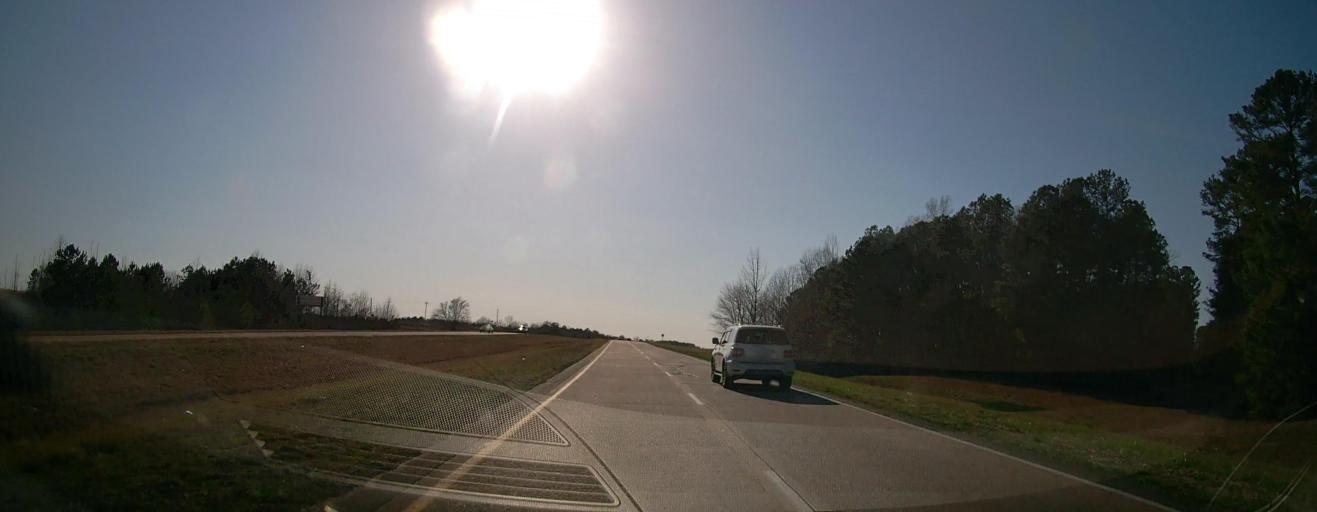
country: US
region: Mississippi
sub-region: Tishomingo County
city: Iuka
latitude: 34.7829
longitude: -88.1659
